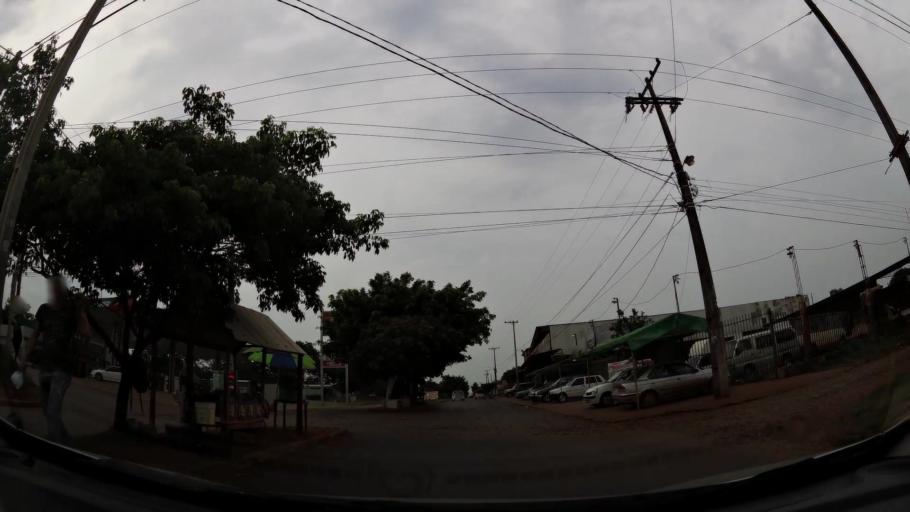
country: PY
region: Alto Parana
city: Presidente Franco
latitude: -25.5334
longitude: -54.6488
